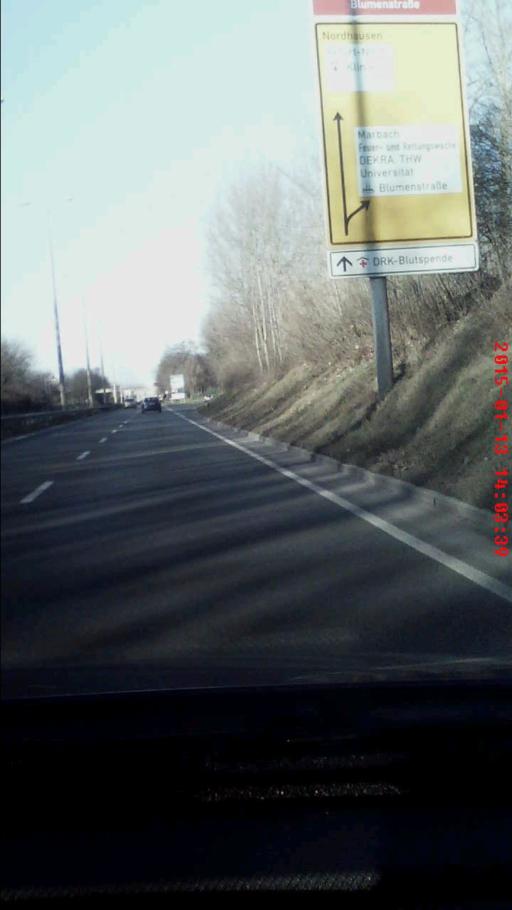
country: DE
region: Thuringia
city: Erfurt
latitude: 50.9783
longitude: 11.0084
